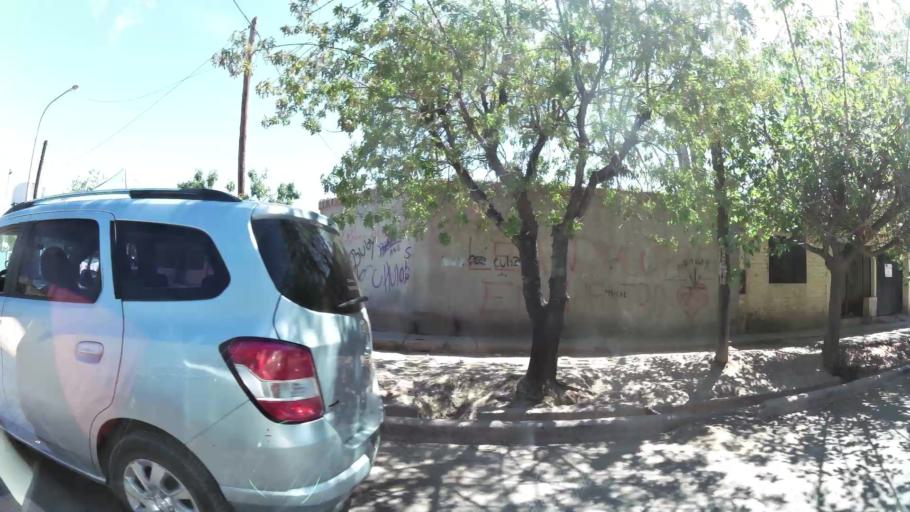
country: AR
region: Mendoza
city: Villa Nueva
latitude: -32.8800
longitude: -68.7982
